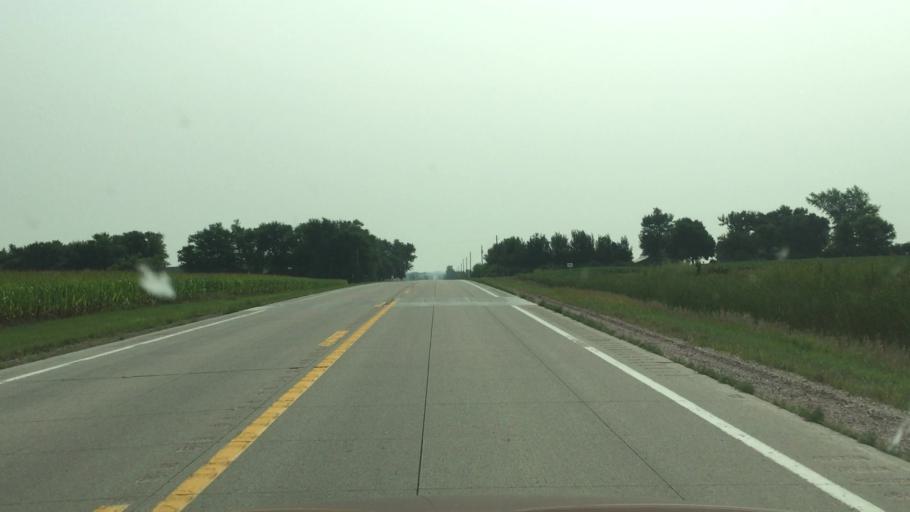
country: US
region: Iowa
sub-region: Osceola County
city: Sibley
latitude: 43.4327
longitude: -95.6655
